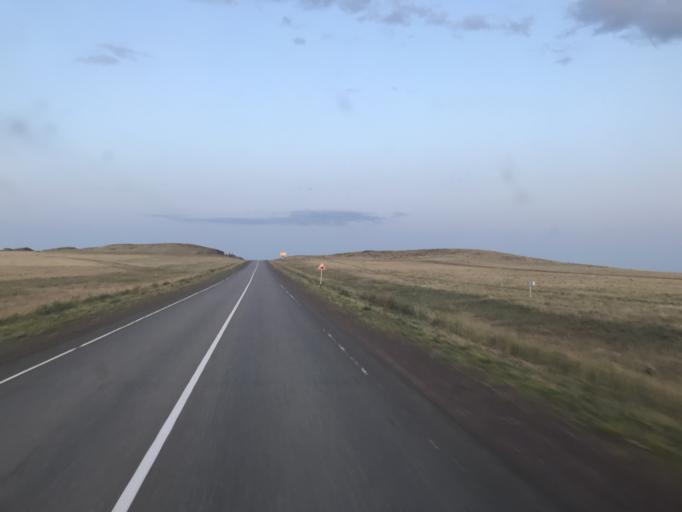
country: KZ
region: Aqmola
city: Astrakhan
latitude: 51.8014
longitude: 69.2132
